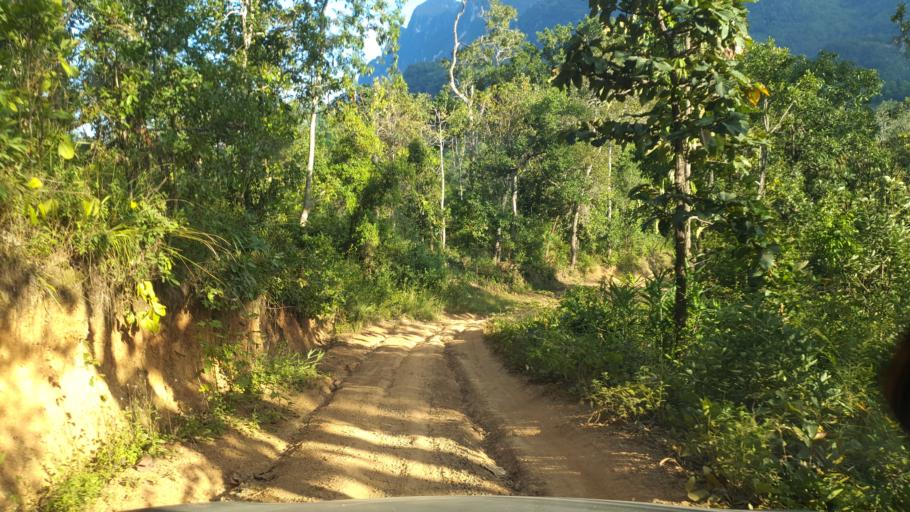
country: TH
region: Chiang Mai
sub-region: Amphoe Chiang Dao
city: Chiang Dao
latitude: 19.4102
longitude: 98.8319
